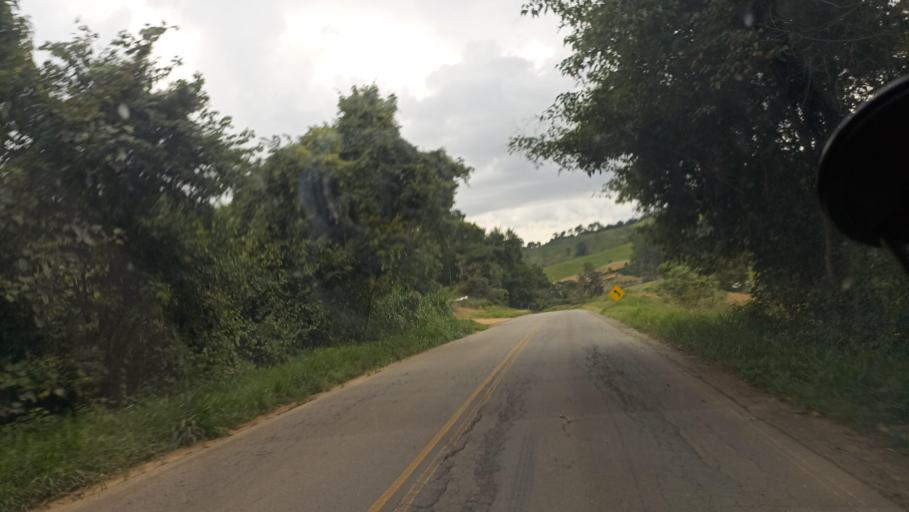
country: BR
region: Minas Gerais
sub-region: Cruzilia
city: Cruzilia
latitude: -21.8799
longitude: -44.8129
